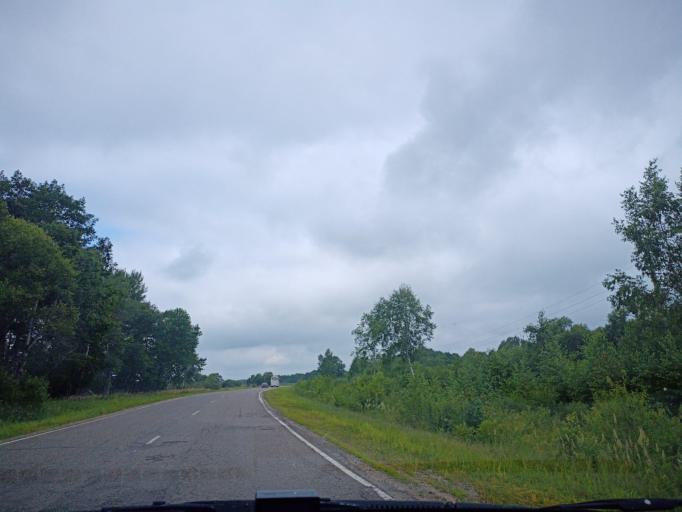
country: RU
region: Primorskiy
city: Novopokrovka
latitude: 45.9713
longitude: 134.2282
